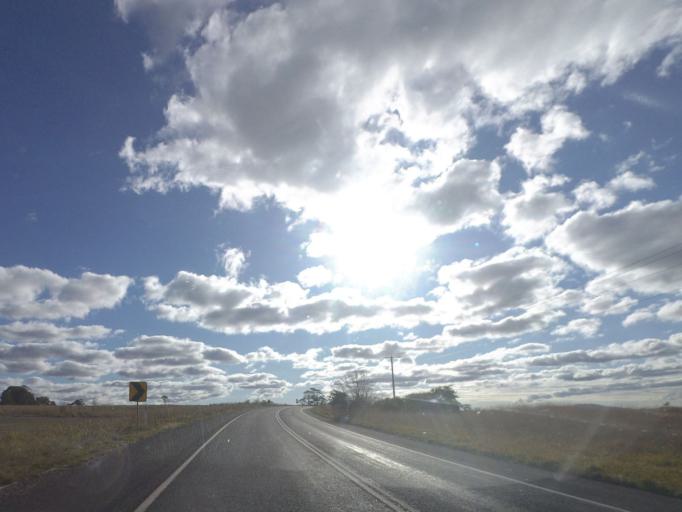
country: AU
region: Victoria
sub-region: Mount Alexander
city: Castlemaine
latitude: -37.1861
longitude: 144.3673
